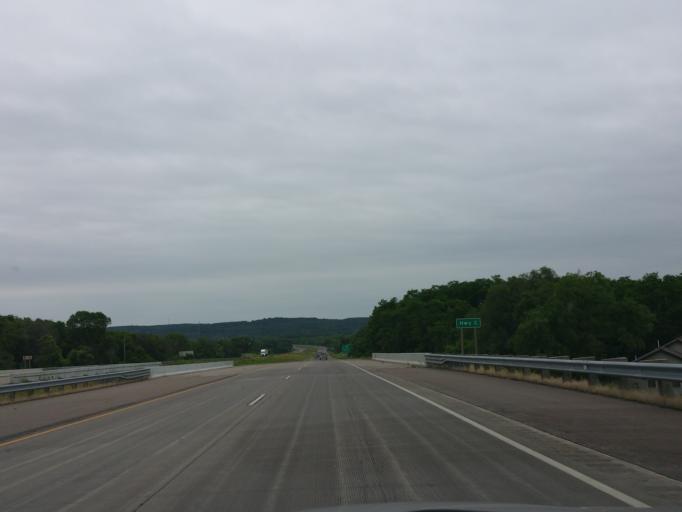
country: US
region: Wisconsin
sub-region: Eau Claire County
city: Eau Claire
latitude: 44.7932
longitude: -91.5499
